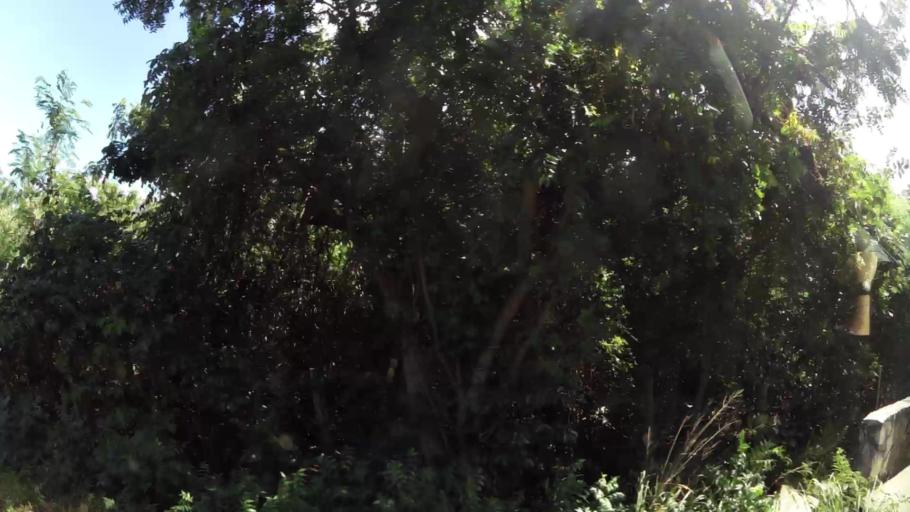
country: VG
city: Tortola
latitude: 18.4334
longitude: -64.4406
